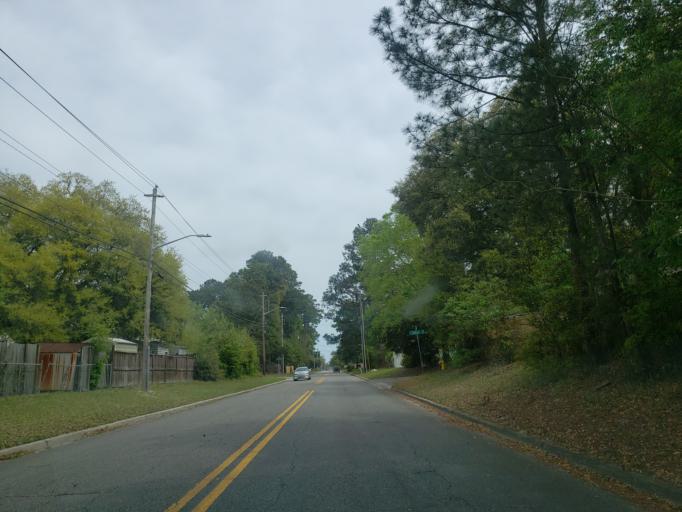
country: US
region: Georgia
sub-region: Chatham County
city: Georgetown
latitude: 31.9911
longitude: -81.1640
